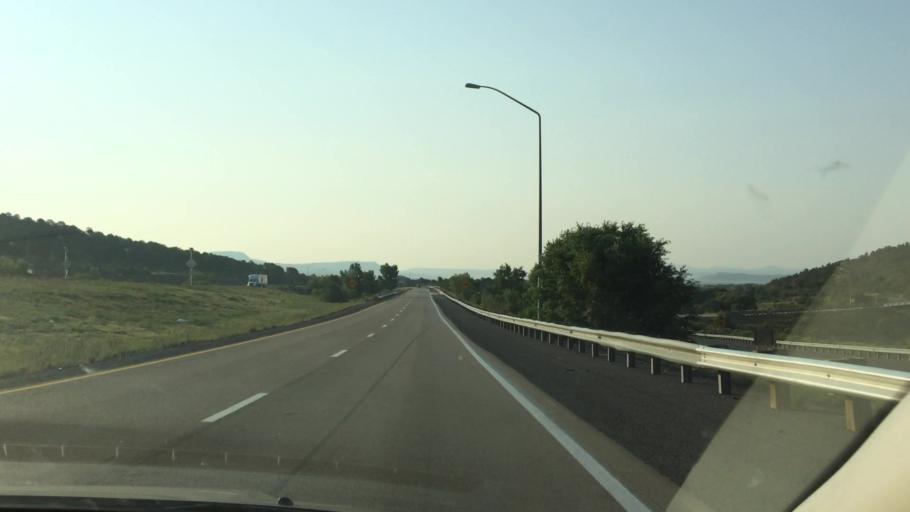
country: US
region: New Mexico
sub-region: Colfax County
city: Raton
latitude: 36.9193
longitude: -104.4484
